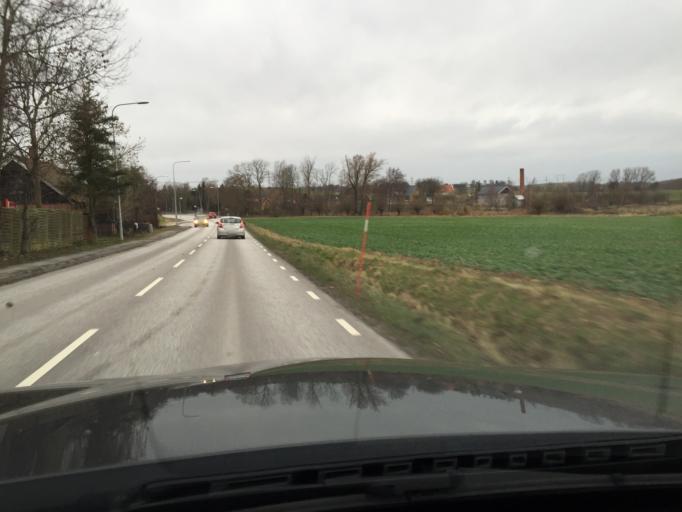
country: SE
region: Skane
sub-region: Malmo
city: Oxie
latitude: 55.5794
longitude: 13.1524
